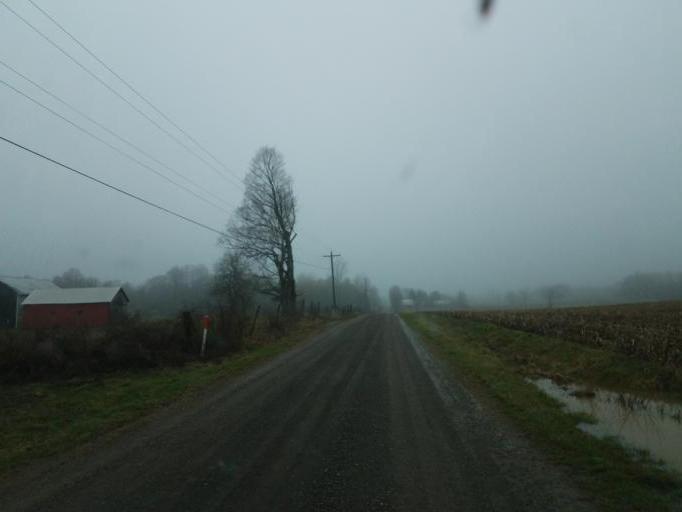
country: US
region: Ohio
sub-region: Richland County
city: Lexington
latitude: 40.6735
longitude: -82.6475
